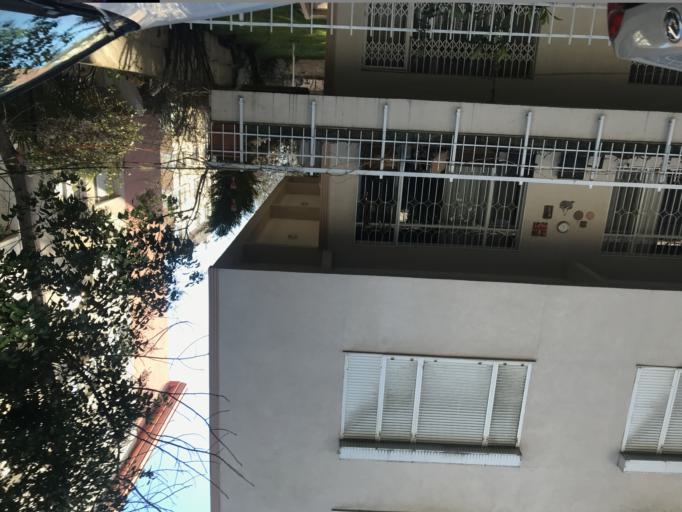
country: TR
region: Istanbul
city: Bahcelievler
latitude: 40.9619
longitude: 28.8338
